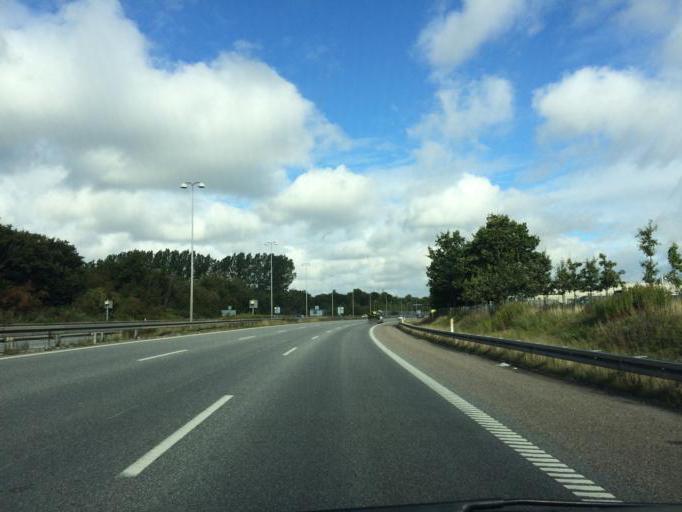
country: DK
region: North Denmark
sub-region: Alborg Kommune
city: Aalborg
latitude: 57.0632
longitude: 9.9493
